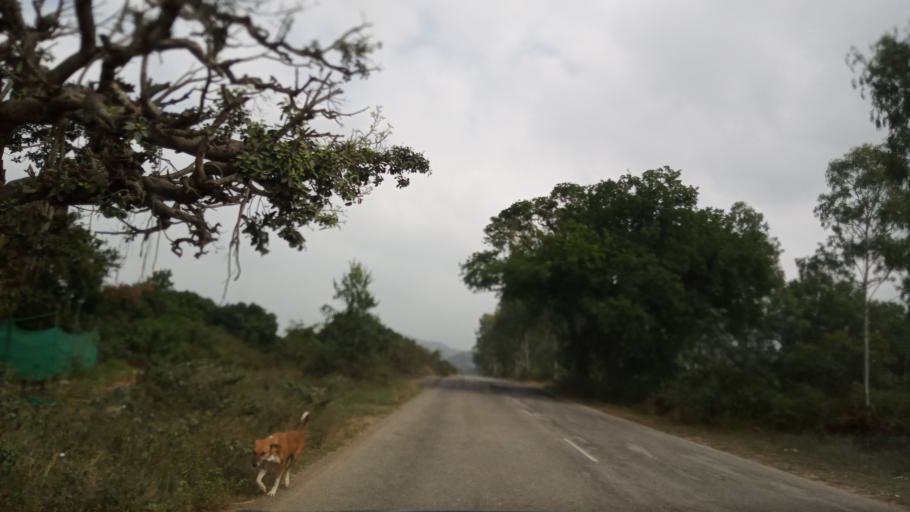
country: IN
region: Andhra Pradesh
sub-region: Chittoor
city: Madanapalle
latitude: 13.5006
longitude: 78.3292
